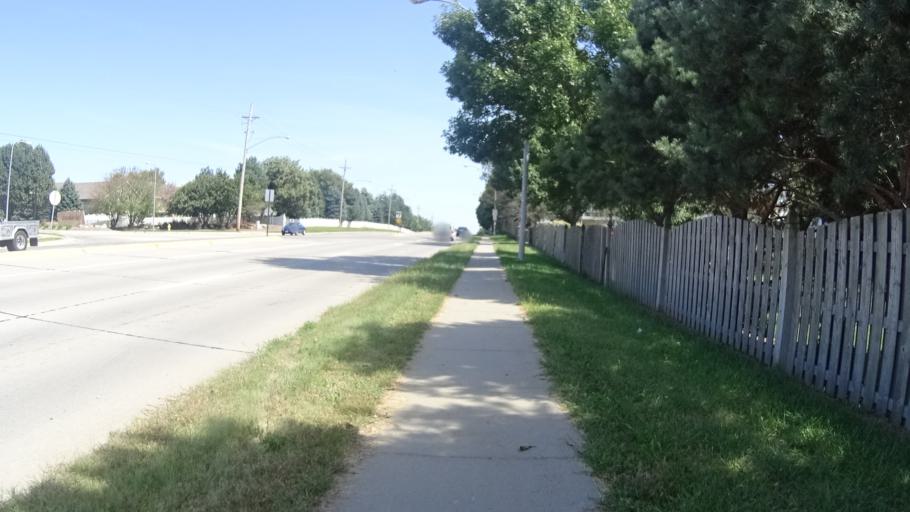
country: US
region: Nebraska
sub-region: Sarpy County
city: Papillion
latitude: 41.1761
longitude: -96.0593
